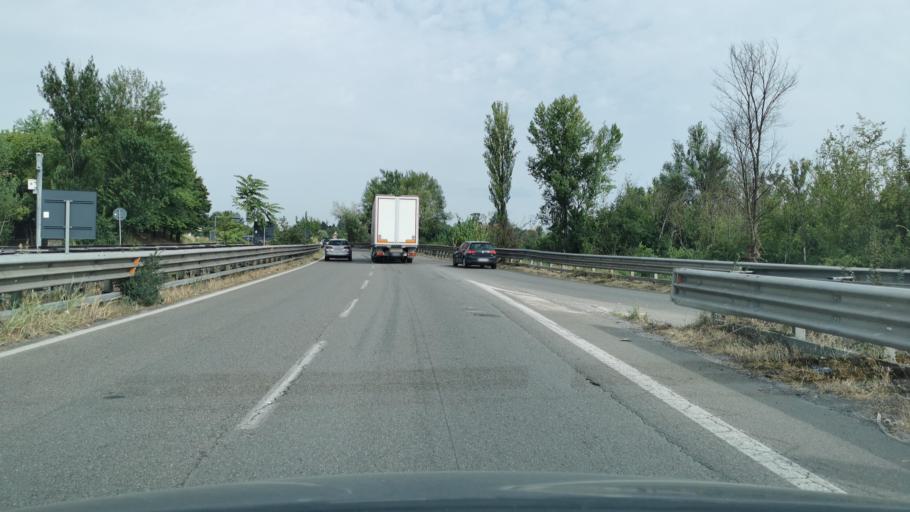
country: IT
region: Emilia-Romagna
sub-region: Provincia di Modena
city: Modena
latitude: 44.6584
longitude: 10.9531
